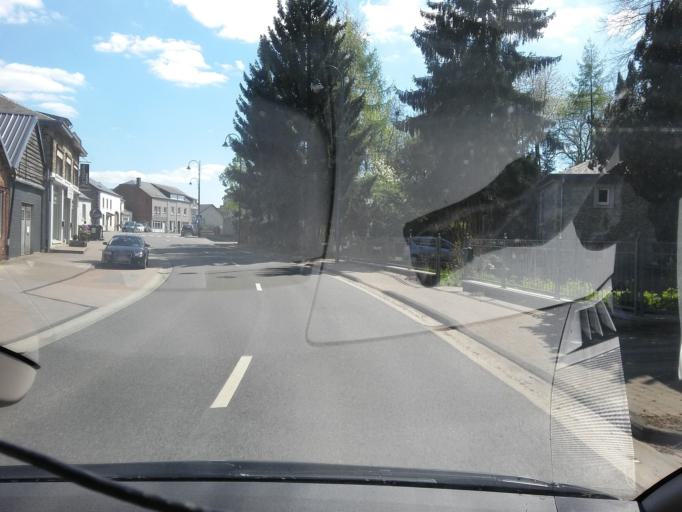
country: BE
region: Wallonia
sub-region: Province du Luxembourg
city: Libin
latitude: 49.9841
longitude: 5.2545
